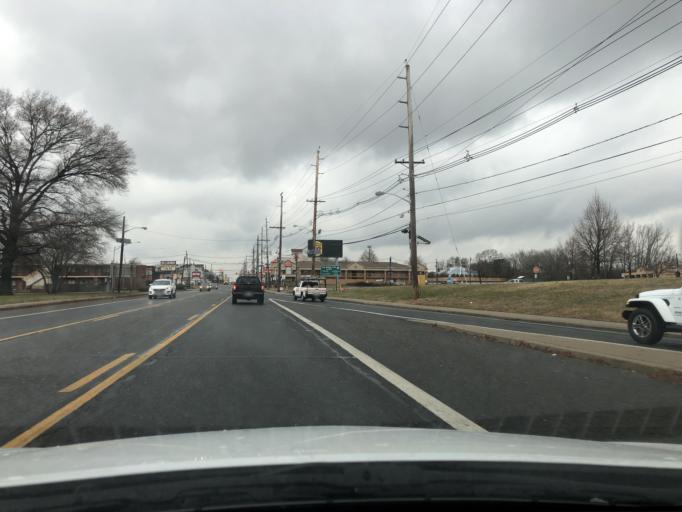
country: US
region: New Jersey
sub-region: Camden County
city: Runnemede
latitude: 39.8619
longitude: -75.0774
